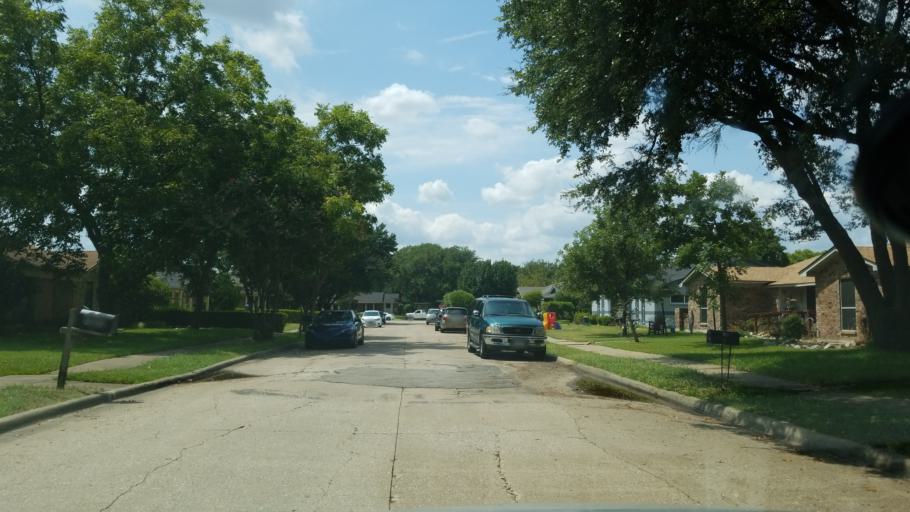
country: US
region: Texas
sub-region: Dallas County
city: Garland
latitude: 32.9284
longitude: -96.6560
